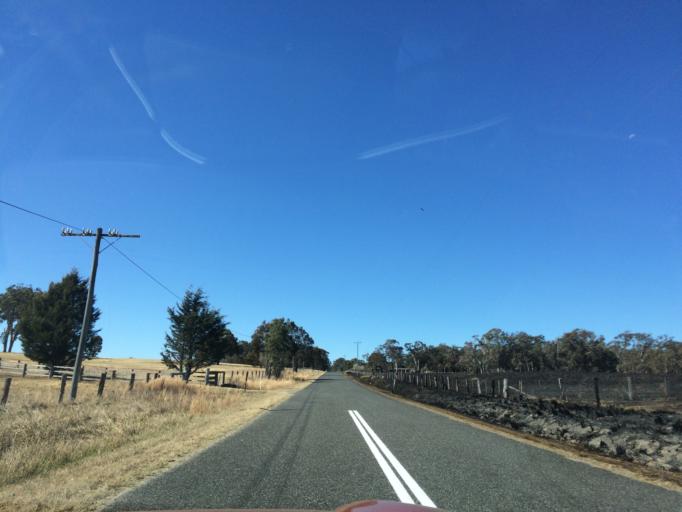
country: AU
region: Queensland
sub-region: Southern Downs
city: Stanthorpe
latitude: -28.6954
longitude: 152.0150
